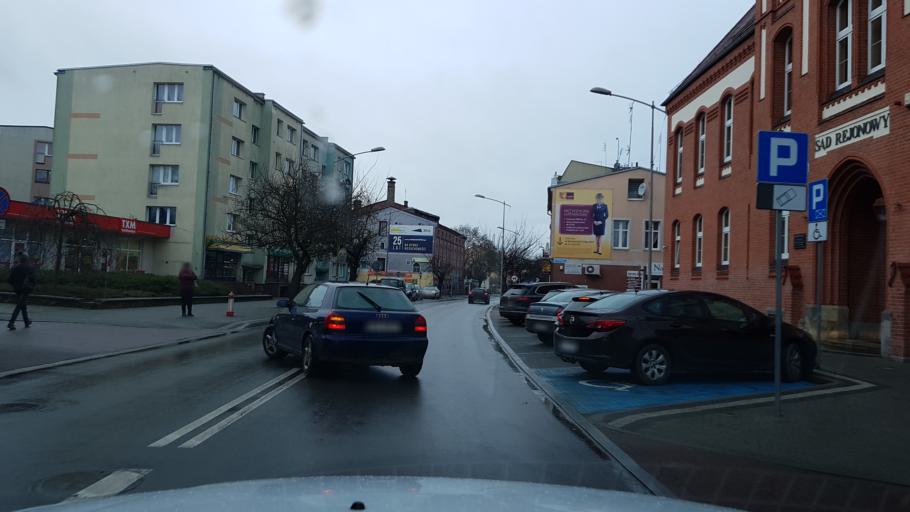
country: PL
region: West Pomeranian Voivodeship
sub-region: Powiat goleniowski
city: Goleniow
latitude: 53.5605
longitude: 14.8360
